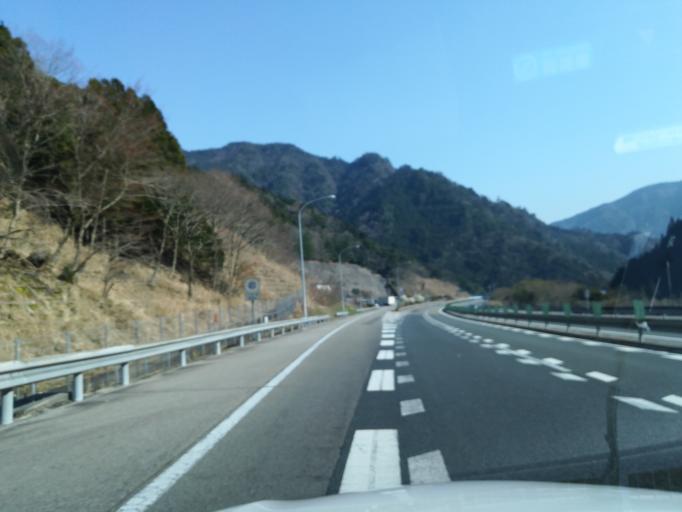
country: JP
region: Ehime
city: Kawanoecho
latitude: 33.9090
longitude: 133.6299
